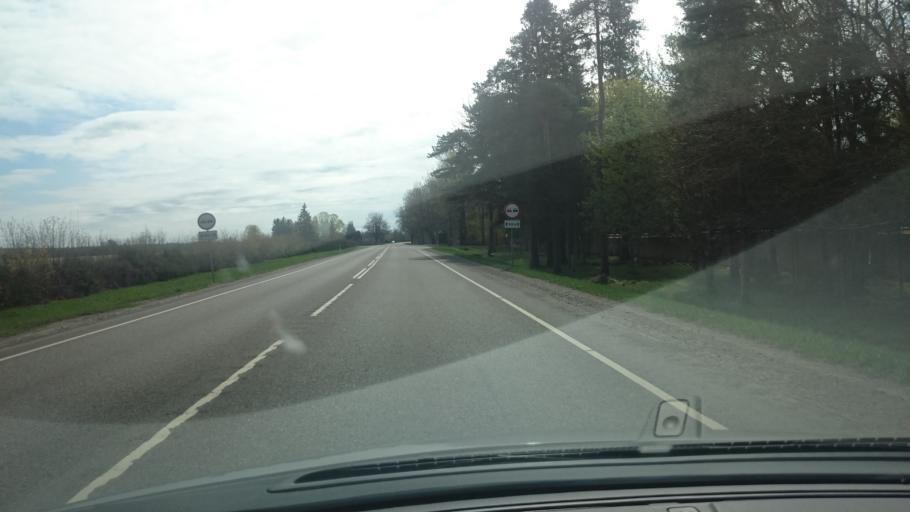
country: EE
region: Laeaene-Virumaa
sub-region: Rakvere linn
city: Rakvere
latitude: 59.3963
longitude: 26.3795
